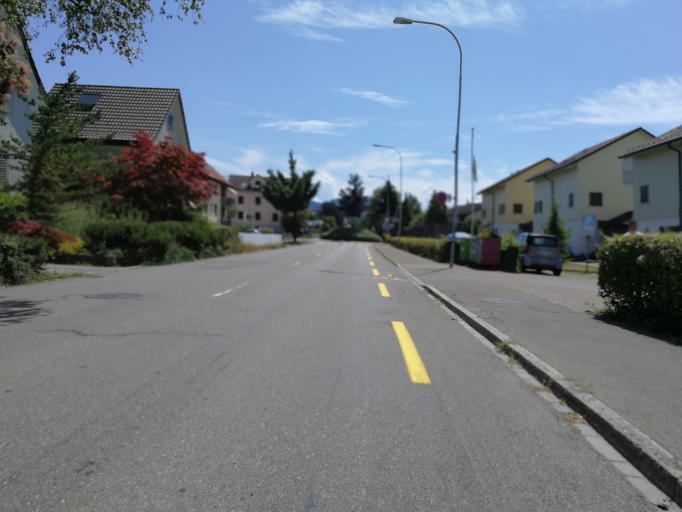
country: CH
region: Zurich
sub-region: Bezirk Hinwil
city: Wetzikon / Ober-Wetzikon
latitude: 47.3253
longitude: 8.8064
